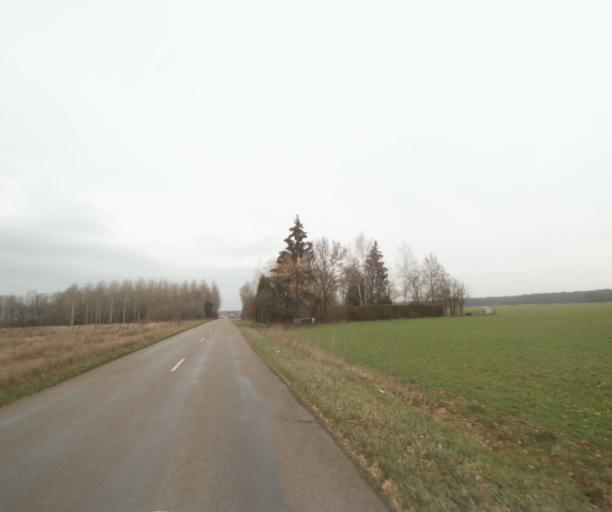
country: FR
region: Champagne-Ardenne
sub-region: Departement de la Haute-Marne
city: Villiers-en-Lieu
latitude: 48.6716
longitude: 4.8919
